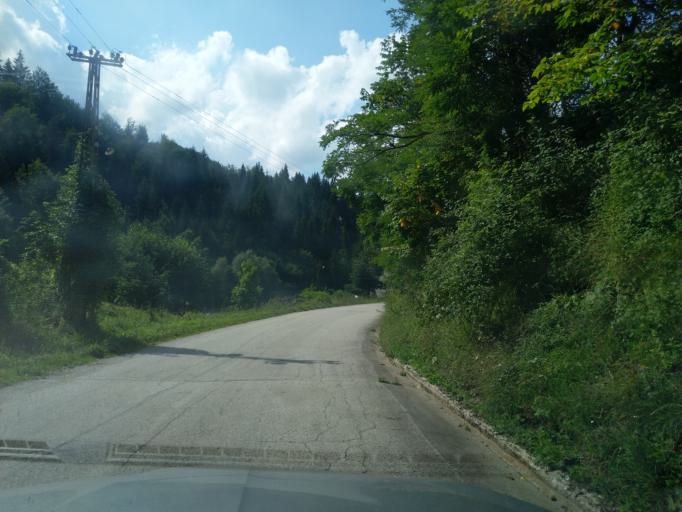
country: RS
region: Central Serbia
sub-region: Zlatiborski Okrug
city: Nova Varos
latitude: 43.5881
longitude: 19.8634
